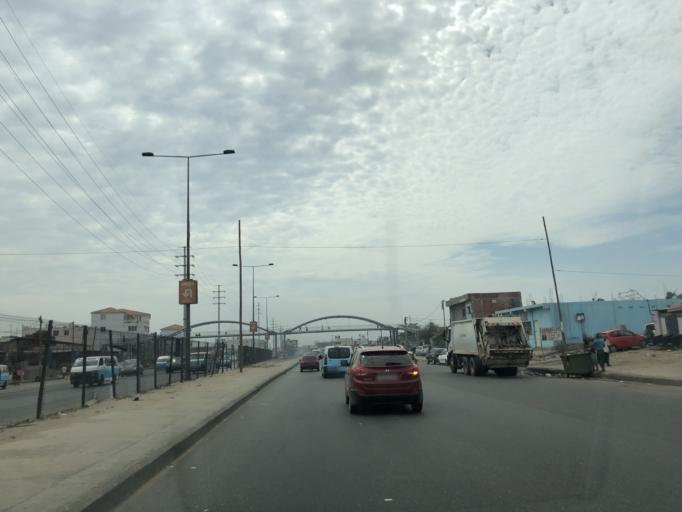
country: AO
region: Luanda
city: Luanda
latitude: -8.8463
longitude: 13.2799
